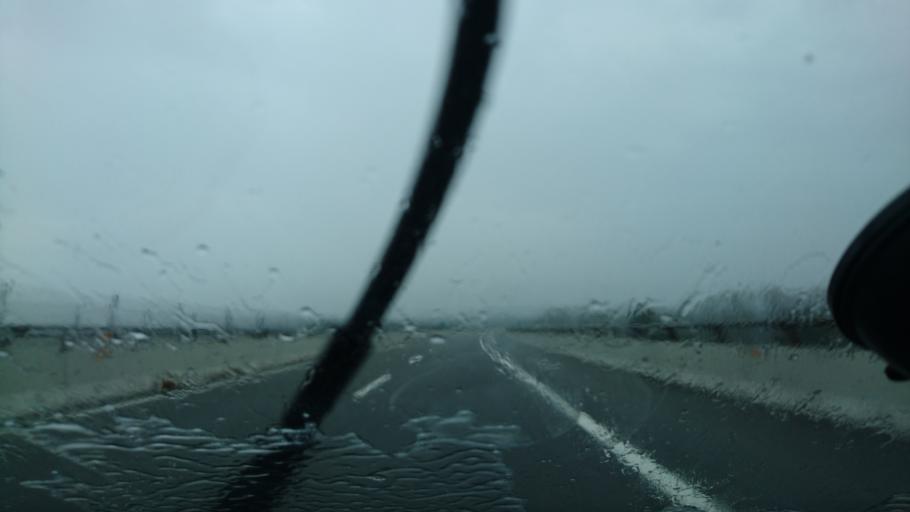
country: IT
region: Piedmont
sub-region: Provincia di Novara
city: Fontaneto D'Agogna
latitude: 45.6503
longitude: 8.4683
